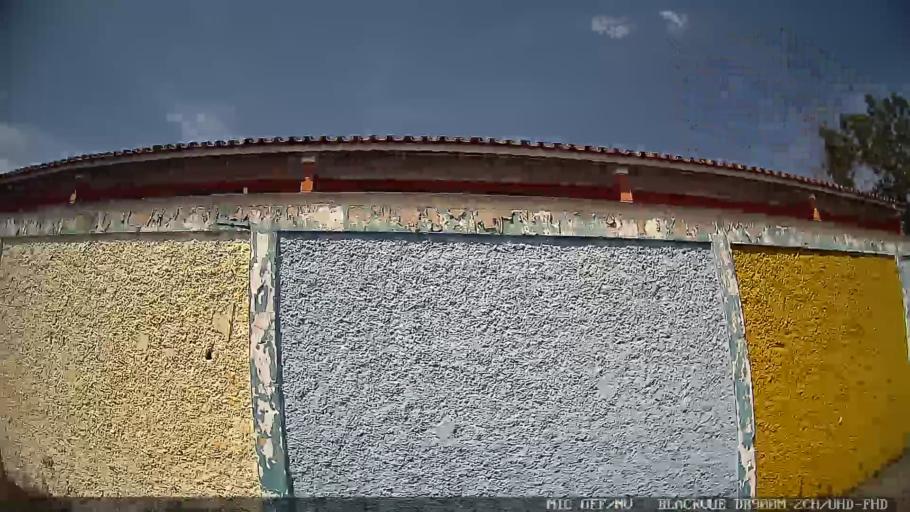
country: BR
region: Sao Paulo
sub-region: Cabreuva
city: Cabreuva
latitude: -23.2479
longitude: -47.0601
